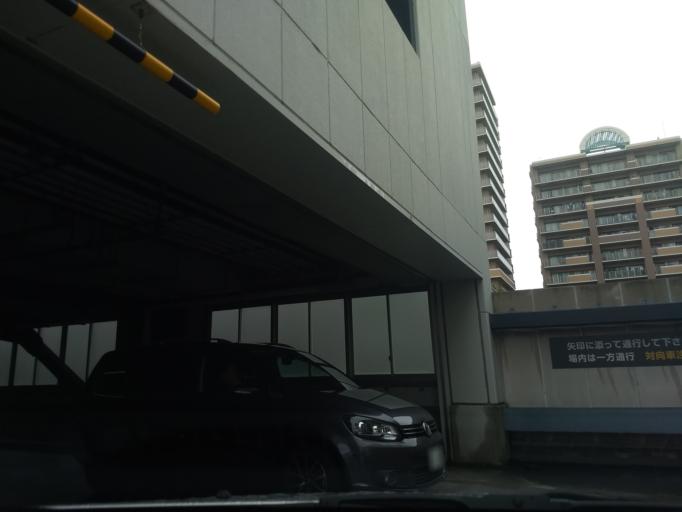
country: JP
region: Tokyo
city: Urayasu
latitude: 35.6366
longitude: 139.9182
